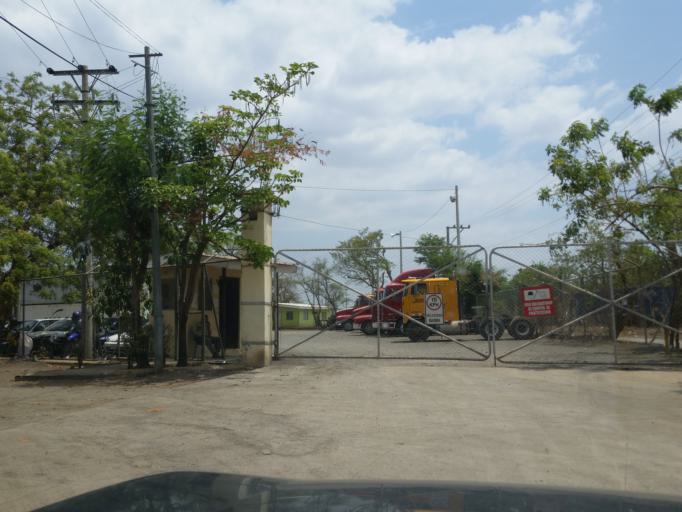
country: NI
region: Managua
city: Managua
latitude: 12.1224
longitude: -86.1649
